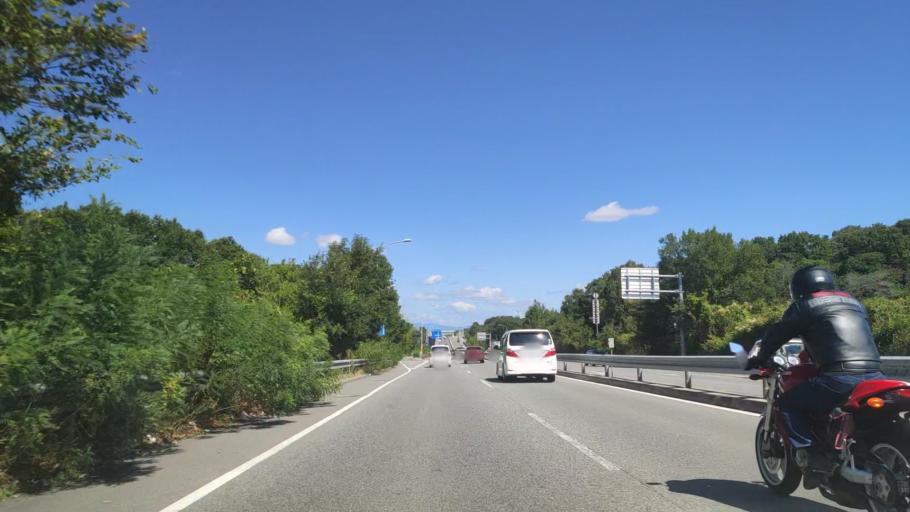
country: JP
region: Hyogo
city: Ono
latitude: 34.8300
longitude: 134.9491
